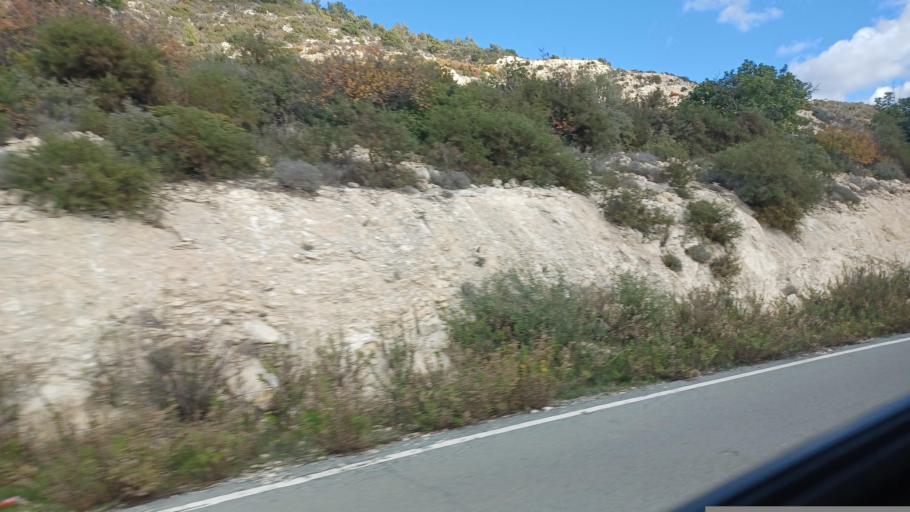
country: CY
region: Limassol
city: Pano Polemidia
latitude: 34.7940
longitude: 32.9810
